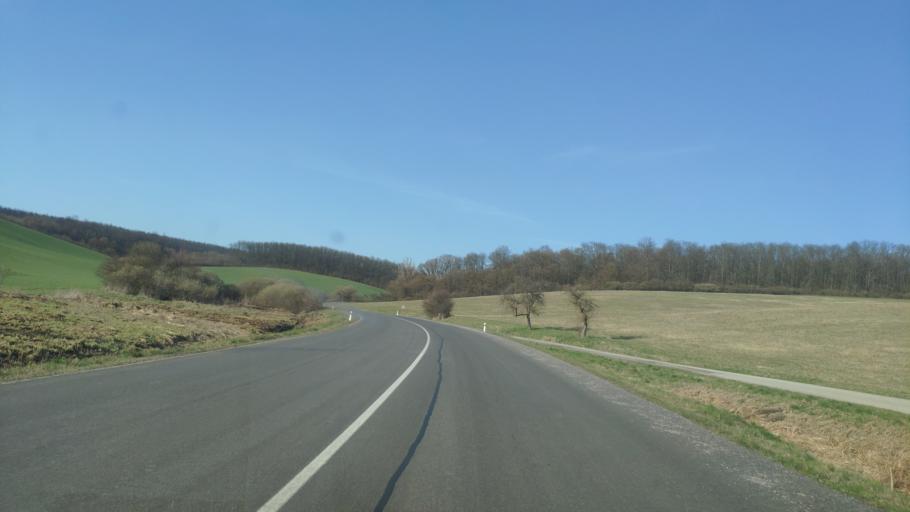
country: HU
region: Borsod-Abauj-Zemplen
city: Putnok
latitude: 48.4915
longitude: 20.2802
